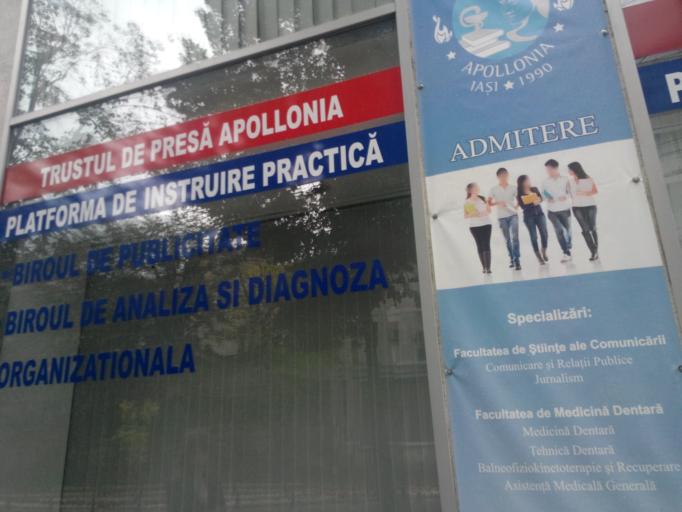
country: RO
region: Iasi
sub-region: Municipiul Iasi
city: Iasi
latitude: 47.1650
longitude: 27.5804
